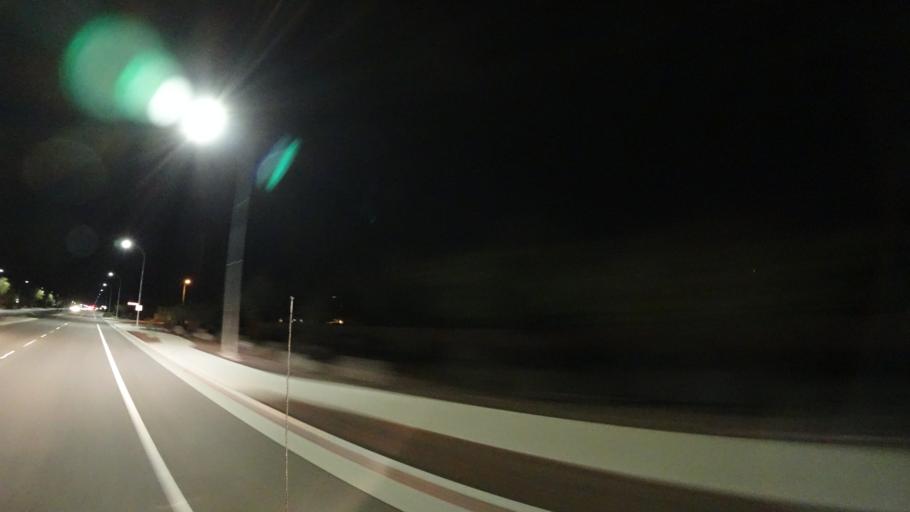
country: US
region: Arizona
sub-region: Maricopa County
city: Sun Lakes
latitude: 33.2441
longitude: -111.8242
